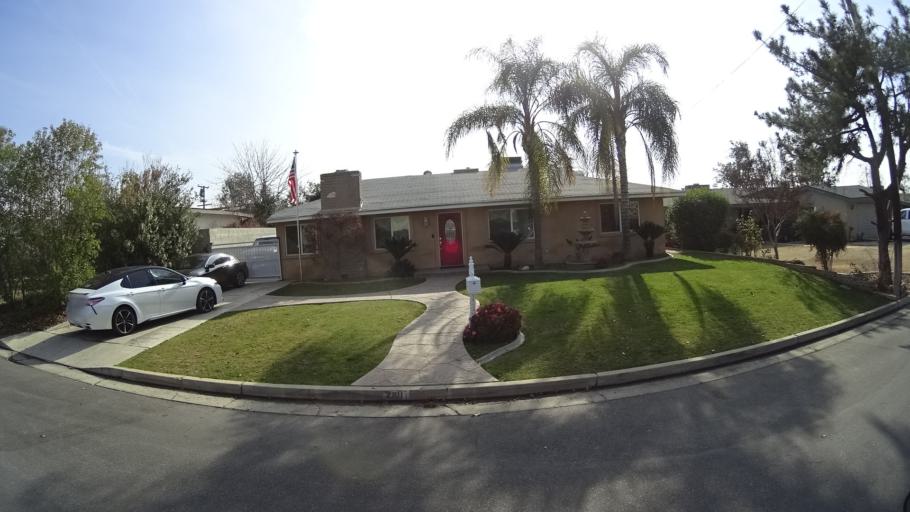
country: US
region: California
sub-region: Kern County
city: Oildale
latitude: 35.4040
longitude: -118.9694
